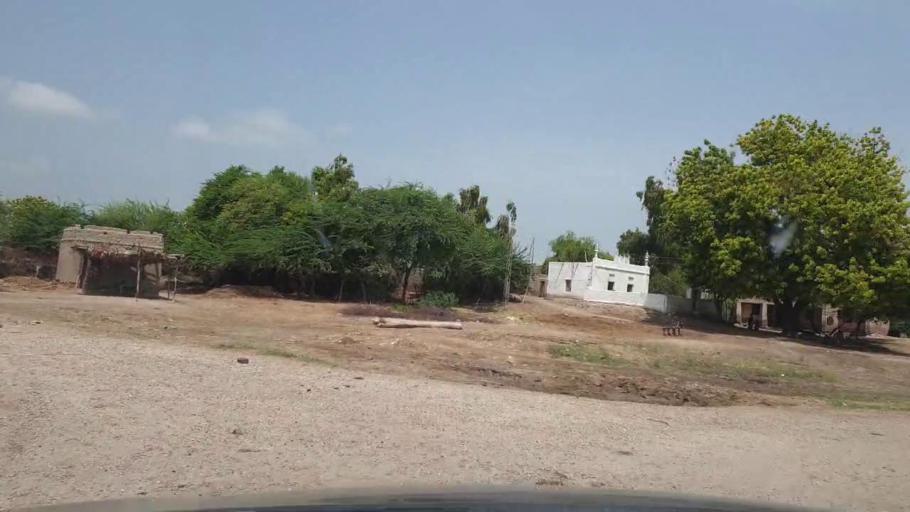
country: PK
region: Sindh
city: Ratodero
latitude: 27.8961
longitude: 68.3148
